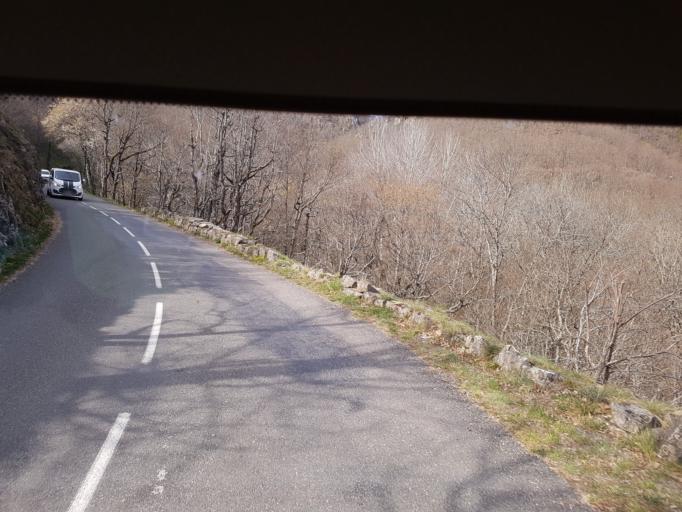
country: FR
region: Languedoc-Roussillon
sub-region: Departement de la Lozere
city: Florac
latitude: 44.3617
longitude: 3.6856
